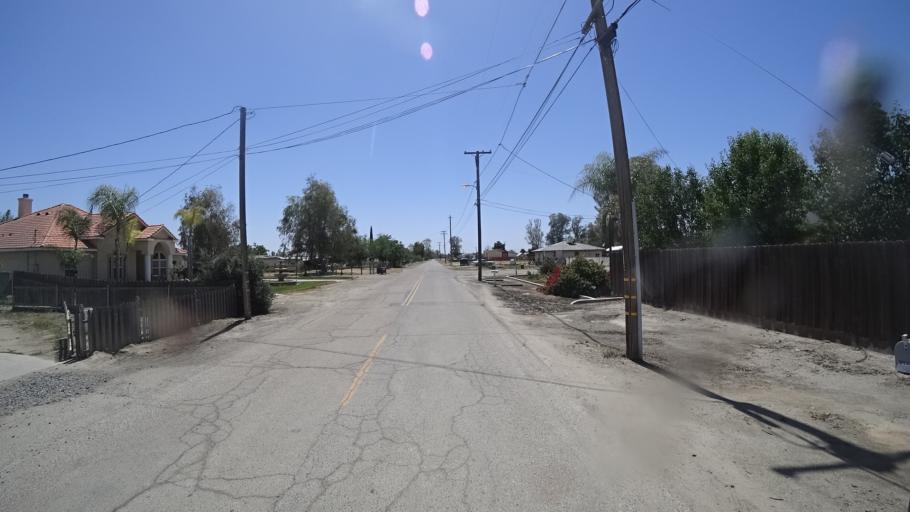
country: US
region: California
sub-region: Kings County
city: Corcoran
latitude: 36.1185
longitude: -119.5767
